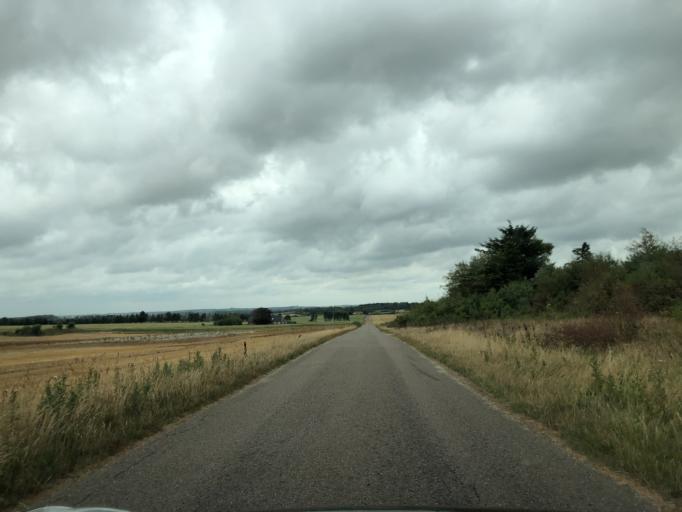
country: DK
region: Central Jutland
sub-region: Ringkobing-Skjern Kommune
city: Skjern
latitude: 56.0878
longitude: 8.4738
